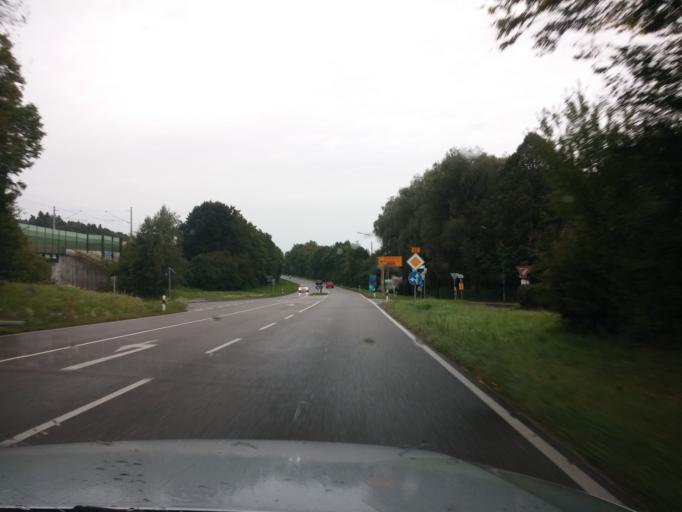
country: DE
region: Bavaria
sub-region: Upper Bavaria
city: Ilmmunster
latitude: 48.4846
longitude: 11.5109
